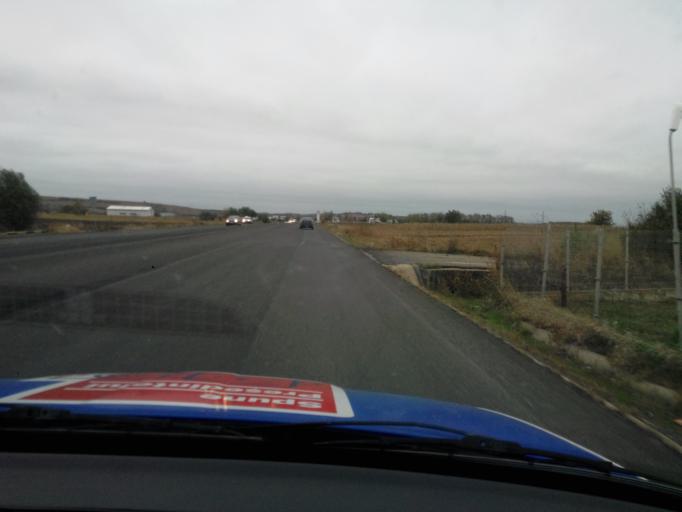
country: RO
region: Giurgiu
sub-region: Comuna Fratesti
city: Fratesti
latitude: 43.9719
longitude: 25.9864
